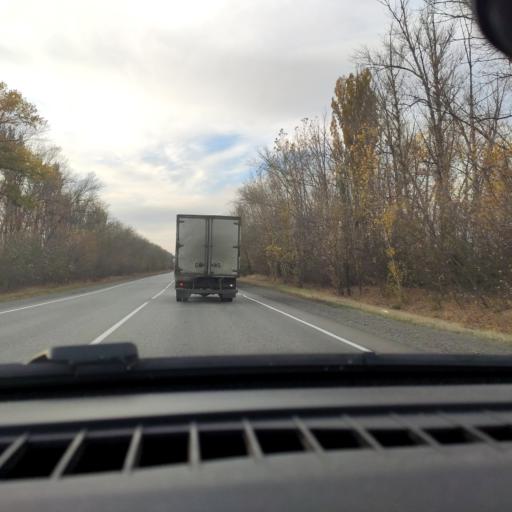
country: RU
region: Voronezj
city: Ostrogozhsk
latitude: 50.9584
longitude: 39.0298
